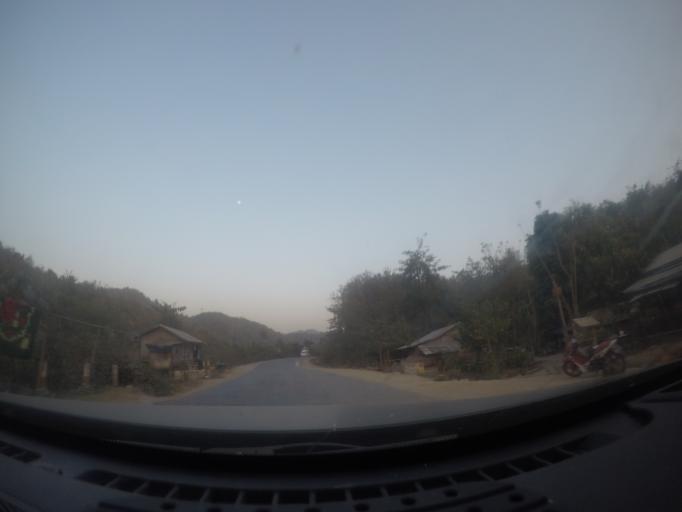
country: MM
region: Mandalay
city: Yamethin
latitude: 20.8256
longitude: 96.4195
